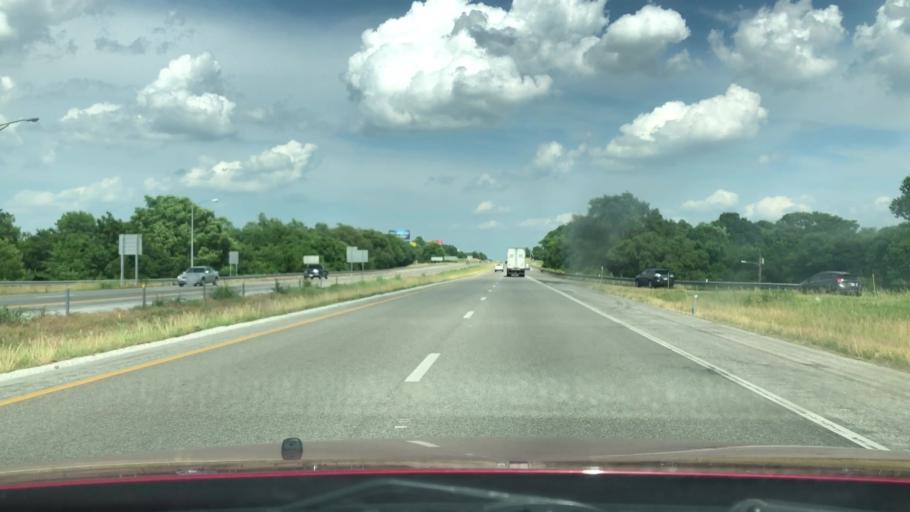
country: US
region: Missouri
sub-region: Greene County
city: Springfield
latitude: 37.2502
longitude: -93.3093
